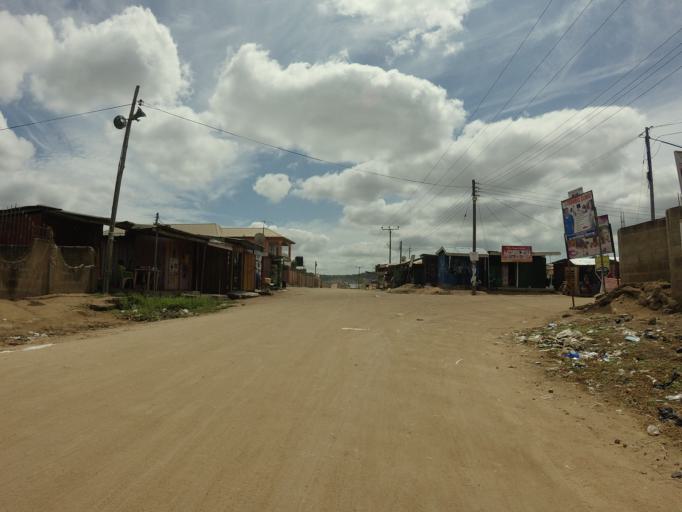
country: GH
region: Central
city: Kasoa
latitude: 5.5461
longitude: -0.4033
